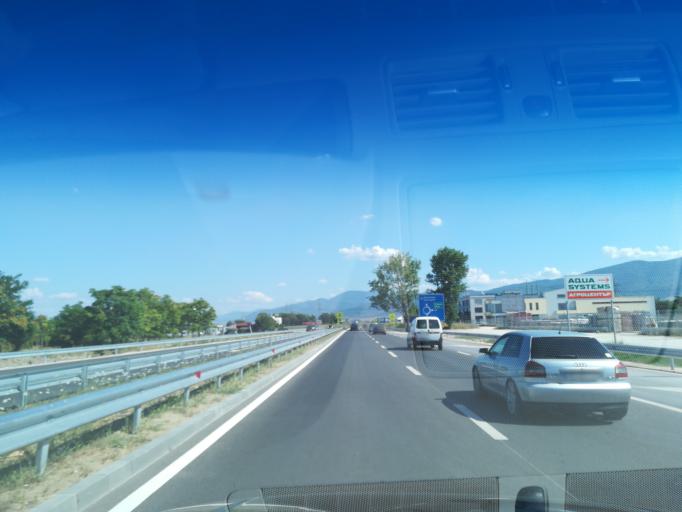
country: BG
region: Plovdiv
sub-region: Obshtina Plovdiv
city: Plovdiv
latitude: 42.1017
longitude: 24.7865
